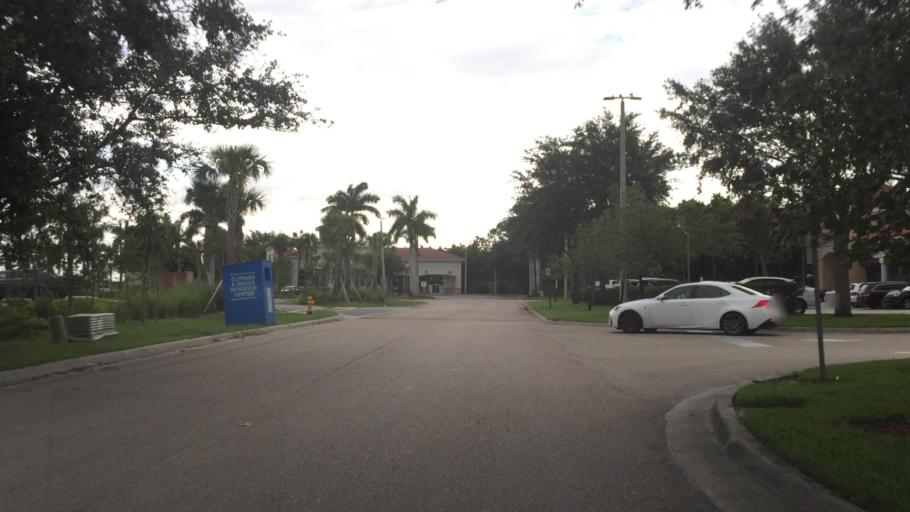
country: US
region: Florida
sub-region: Lee County
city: Estero
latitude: 26.4385
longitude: -81.7703
